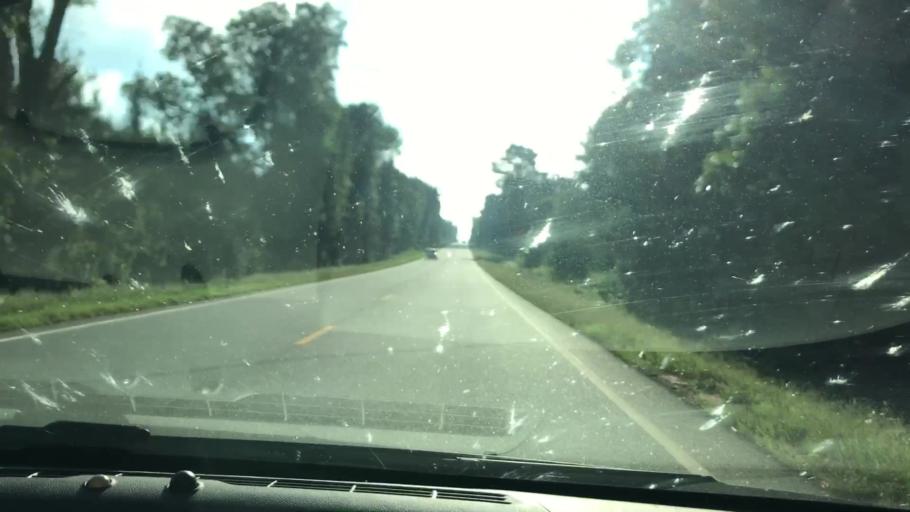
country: US
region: Georgia
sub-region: Terrell County
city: Dawson
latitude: 31.7699
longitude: -84.4915
